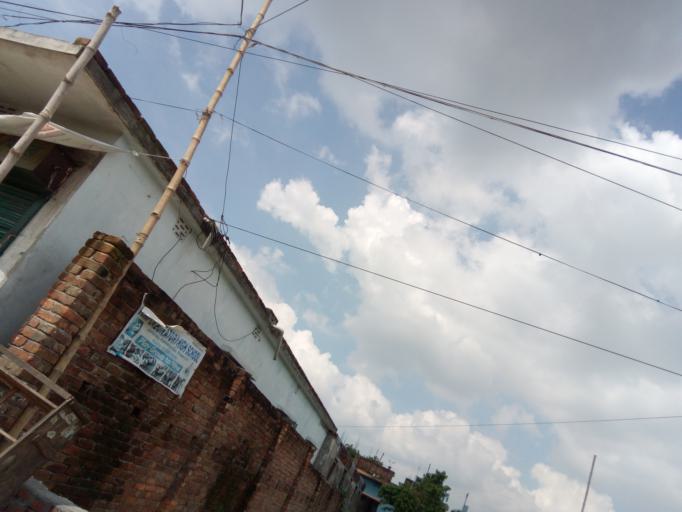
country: BD
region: Dhaka
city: Azimpur
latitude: 23.7282
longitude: 90.3607
